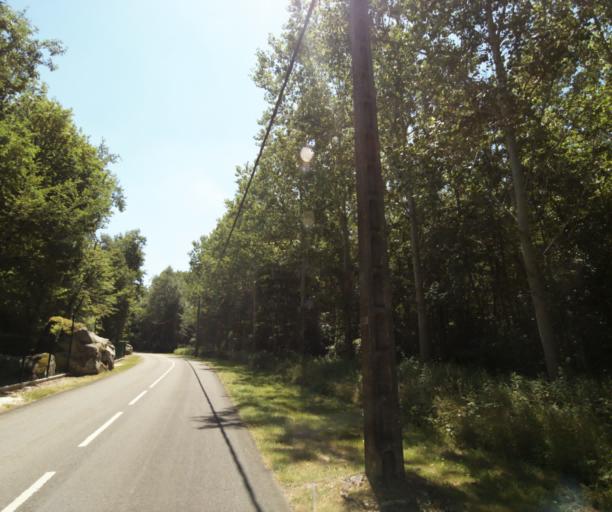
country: FR
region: Centre
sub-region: Departement du Loiret
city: Malesherbes
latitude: 48.2974
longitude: 2.4248
